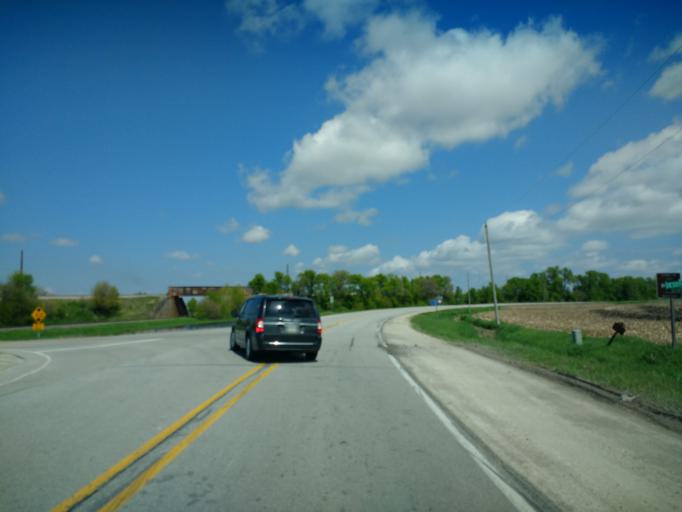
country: US
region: Iowa
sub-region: Harrison County
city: Missouri Valley
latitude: 41.4990
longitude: -95.8935
